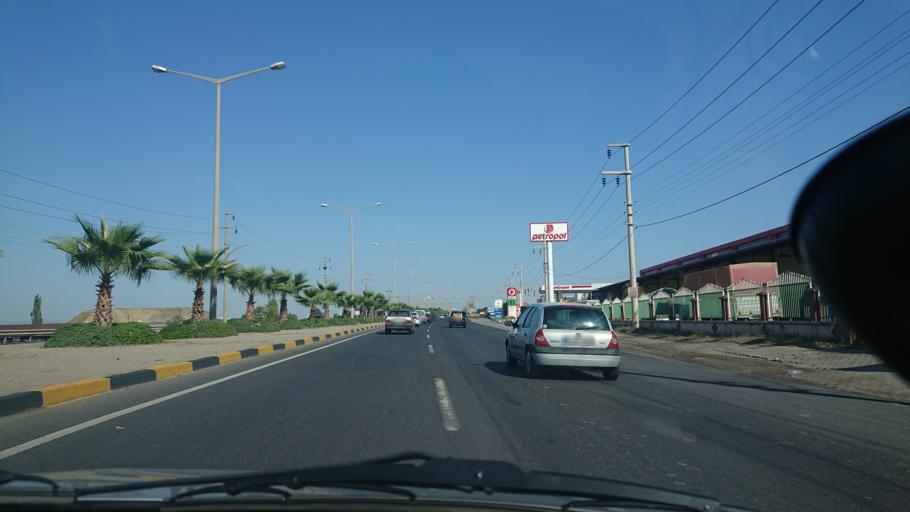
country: TR
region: Manisa
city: Turgutlu
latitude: 38.4957
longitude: 27.7360
